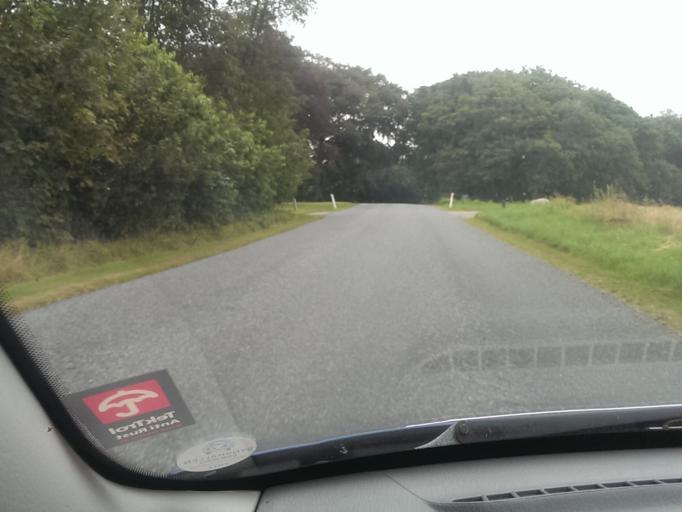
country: DK
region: South Denmark
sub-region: Esbjerg Kommune
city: Tjaereborg
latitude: 55.5138
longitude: 8.5826
